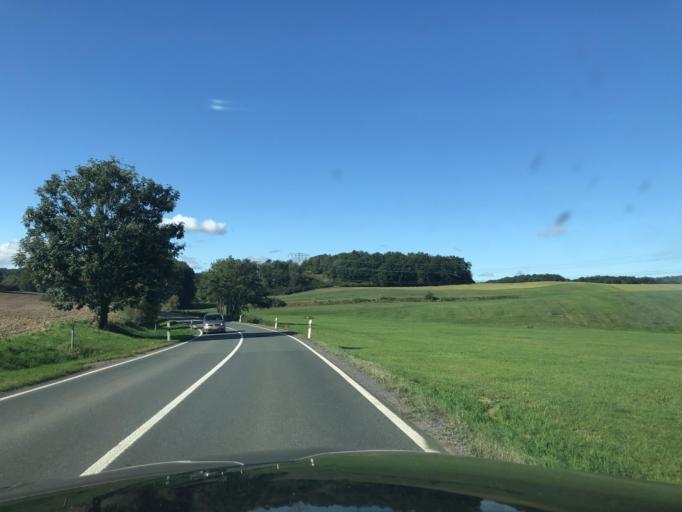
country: DE
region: Thuringia
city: Crimla
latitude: 50.7804
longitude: 12.0354
